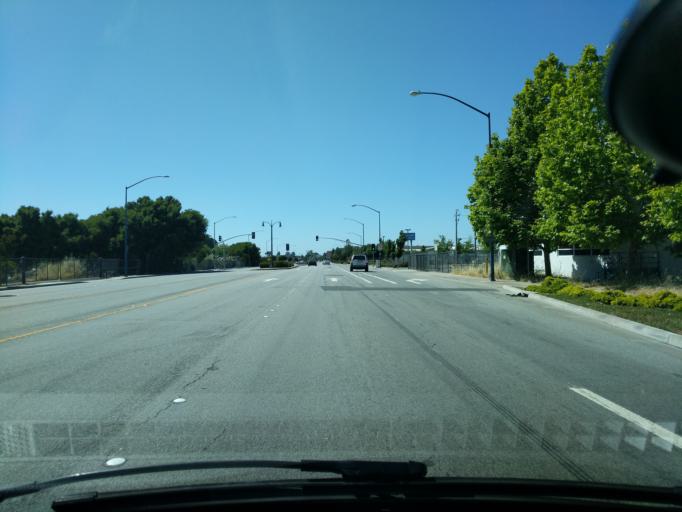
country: US
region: California
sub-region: Alameda County
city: San Leandro
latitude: 37.7216
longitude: -122.1935
